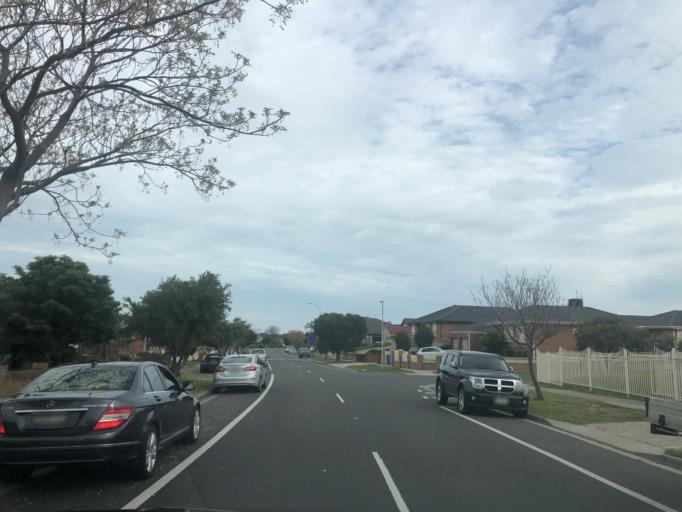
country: AU
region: Victoria
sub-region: Casey
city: Hallam
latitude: -38.0122
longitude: 145.2773
